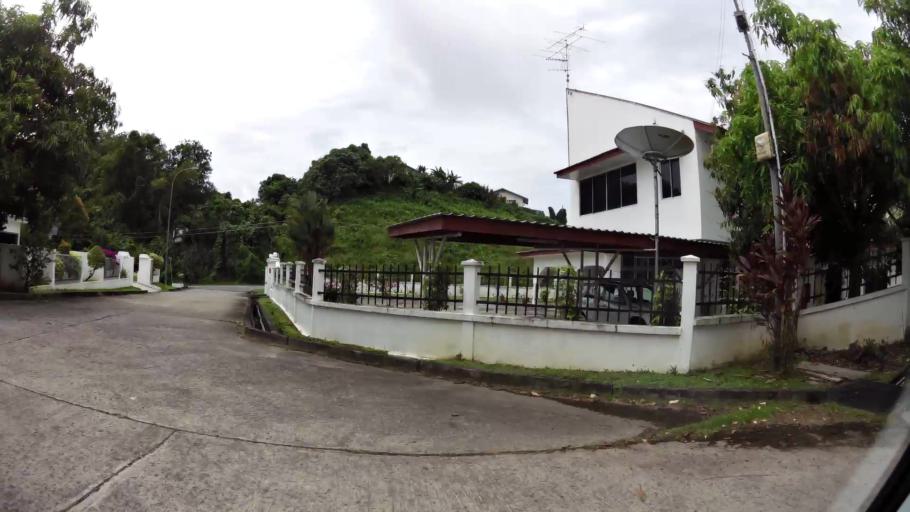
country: BN
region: Brunei and Muara
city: Bandar Seri Begawan
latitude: 4.8895
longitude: 114.9232
